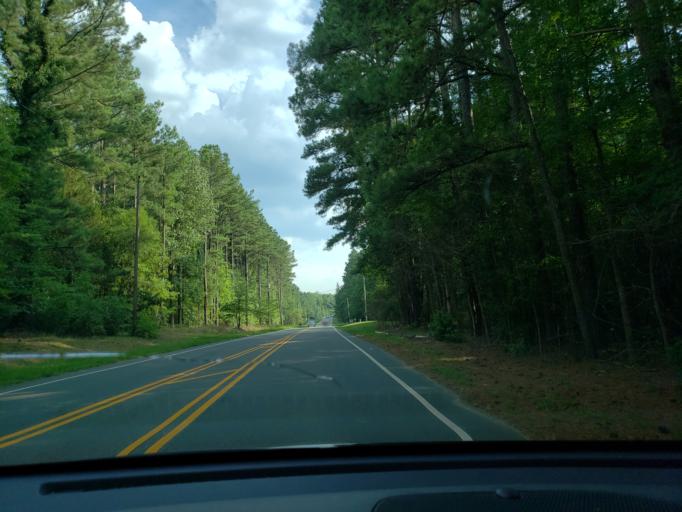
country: US
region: North Carolina
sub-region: Orange County
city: Chapel Hill
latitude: 35.8919
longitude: -78.9812
